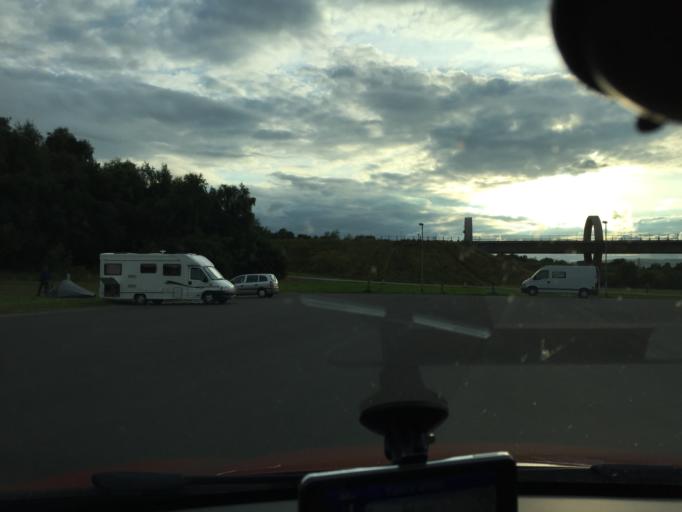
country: GB
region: Scotland
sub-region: Falkirk
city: Larbert
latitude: 55.9993
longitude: -3.8393
